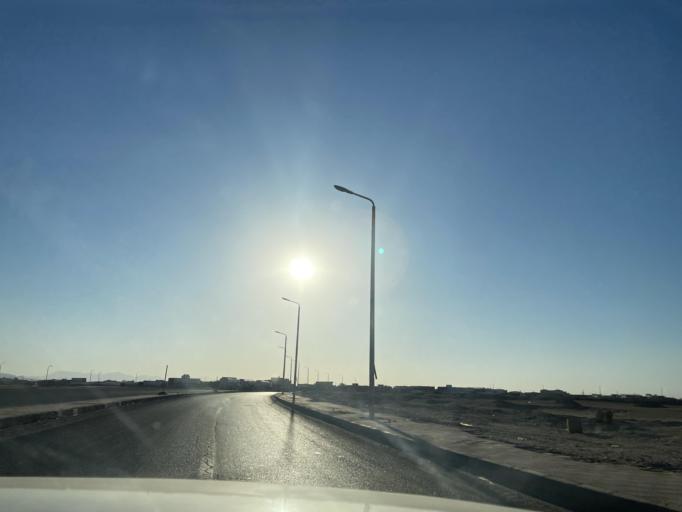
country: EG
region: Red Sea
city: Hurghada
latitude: 27.2189
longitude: 33.7887
